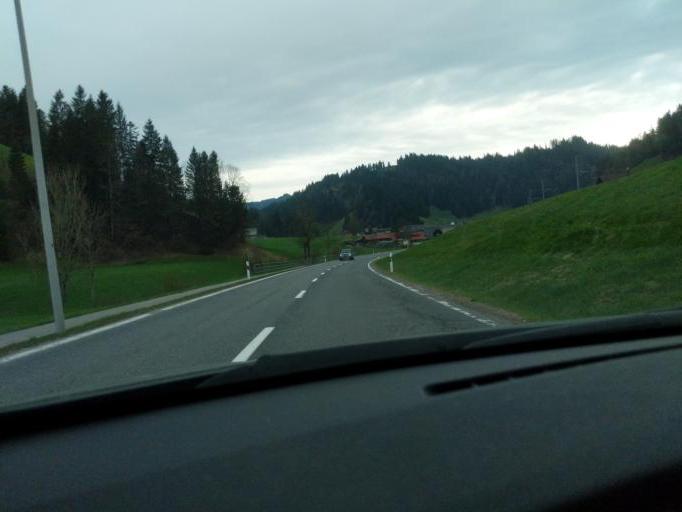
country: CH
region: Lucerne
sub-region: Entlebuch District
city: Escholzmatt
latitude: 46.8997
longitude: 7.9206
